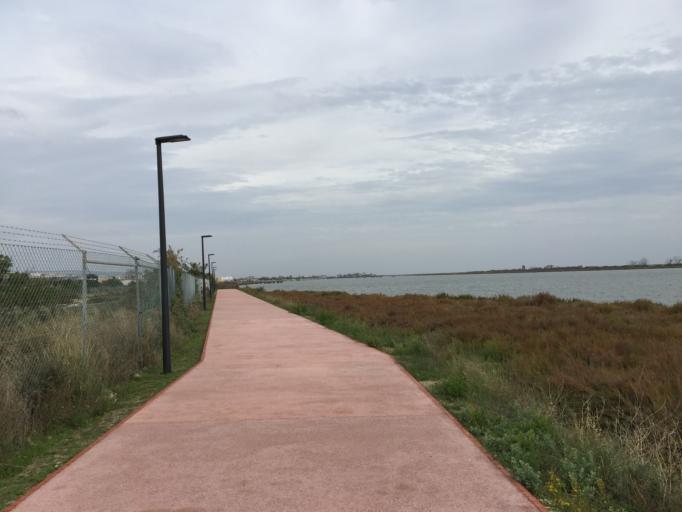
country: PT
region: Lisbon
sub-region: Vila Franca de Xira
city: Povoa de Santa Iria
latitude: 38.8494
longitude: -9.0680
